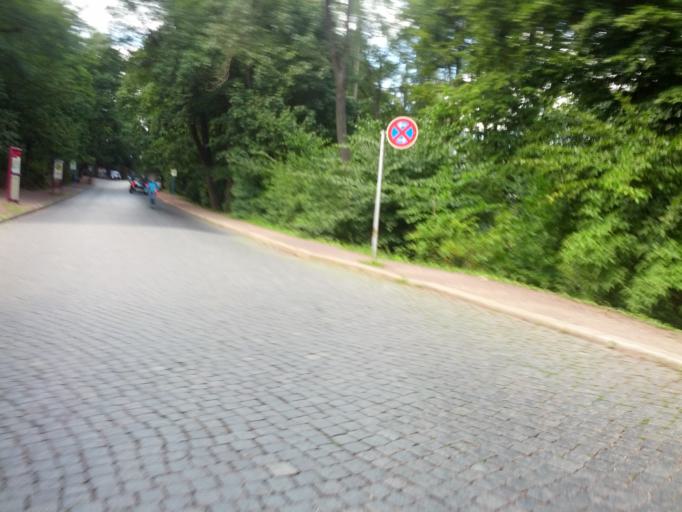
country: DE
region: Thuringia
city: Eisenach
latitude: 50.9684
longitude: 10.3076
